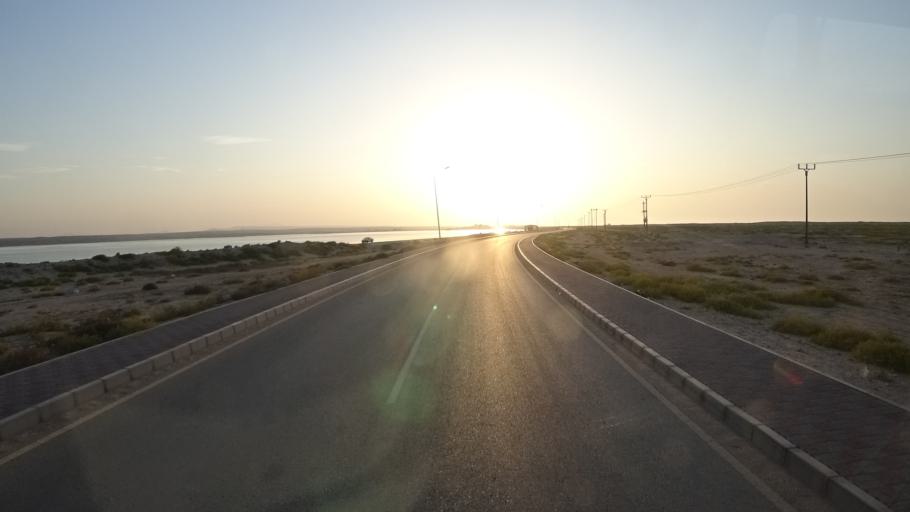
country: OM
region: Ash Sharqiyah
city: Sur
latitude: 22.5272
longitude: 59.7840
